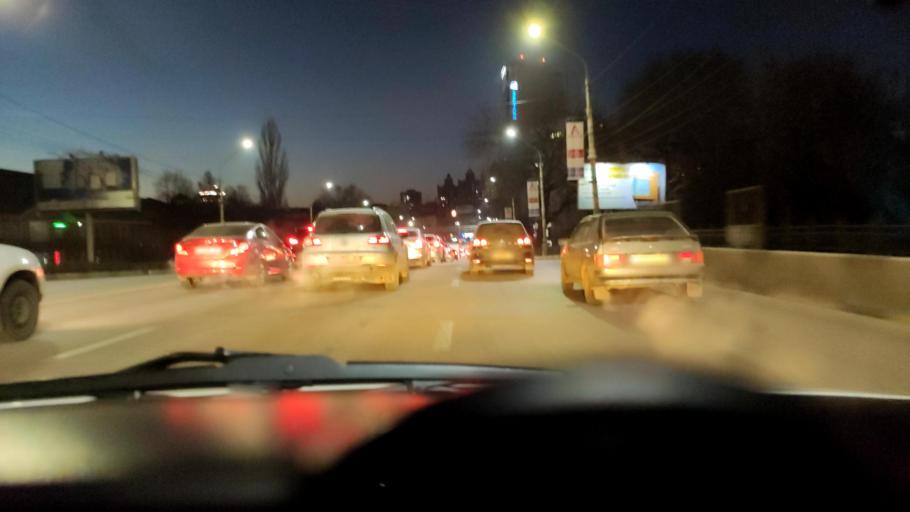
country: RU
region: Voronezj
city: Voronezh
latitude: 51.6762
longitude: 39.1856
